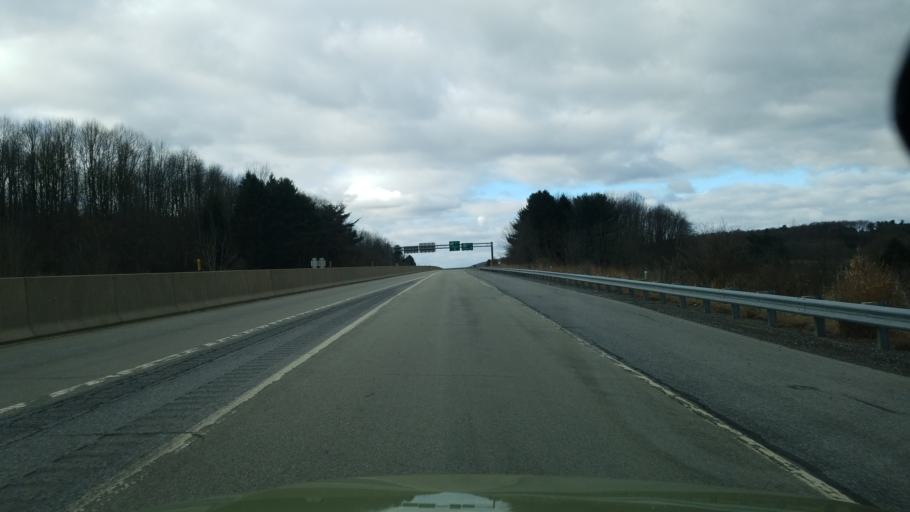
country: US
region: Pennsylvania
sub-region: Indiana County
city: Chevy Chase Heights
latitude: 40.6267
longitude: -79.1202
